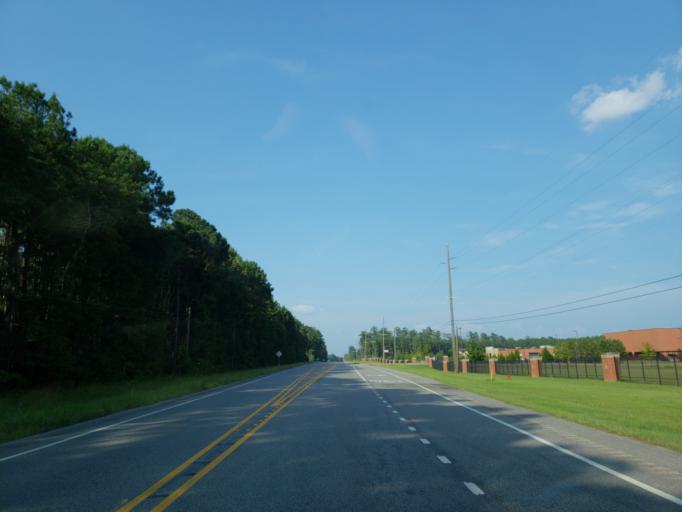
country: US
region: Alabama
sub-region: Sumter County
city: Livingston
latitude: 32.5491
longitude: -88.2320
